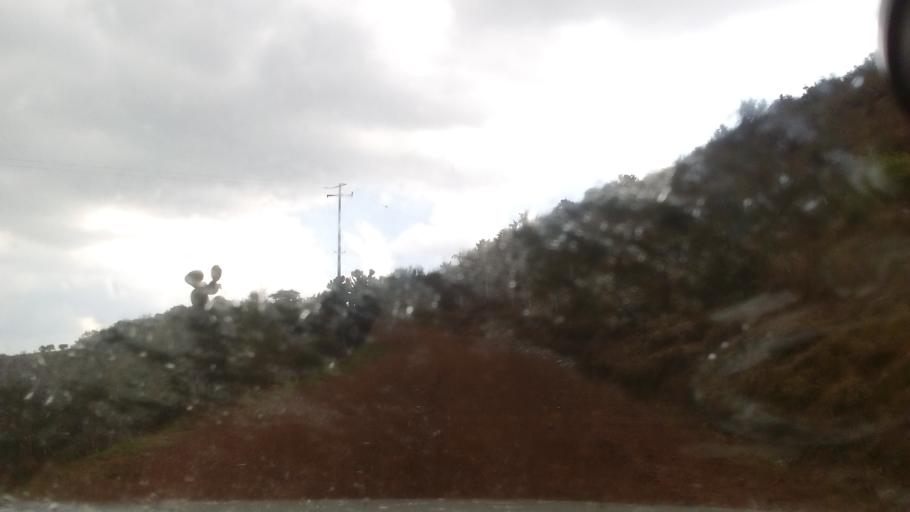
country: MX
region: Guanajuato
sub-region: Silao de la Victoria
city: San Francisco (Banos de Agua Caliente)
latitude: 21.1502
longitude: -101.4371
